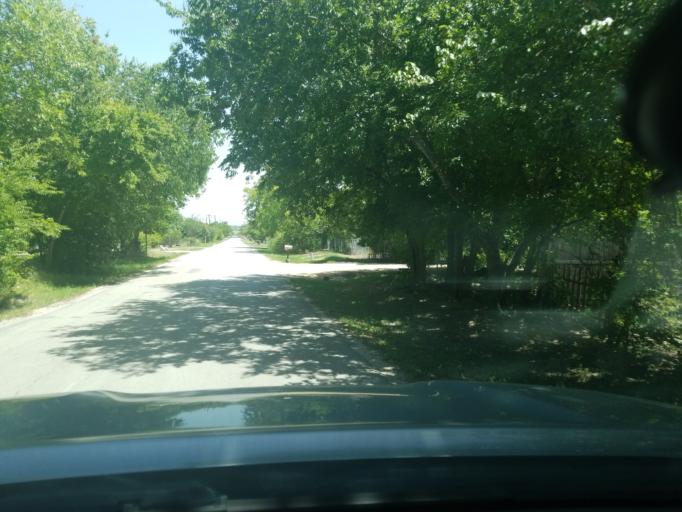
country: US
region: Texas
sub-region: Guadalupe County
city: Cibolo
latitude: 29.5753
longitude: -98.1950
